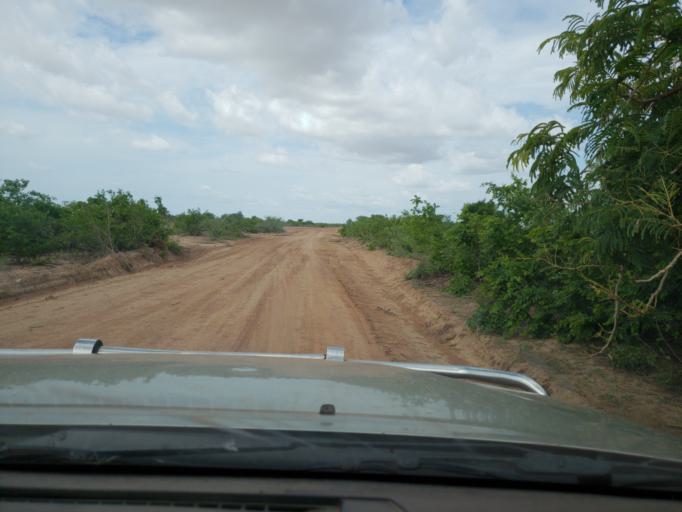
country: ML
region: Segou
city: Bla
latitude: 12.7078
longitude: -5.7039
